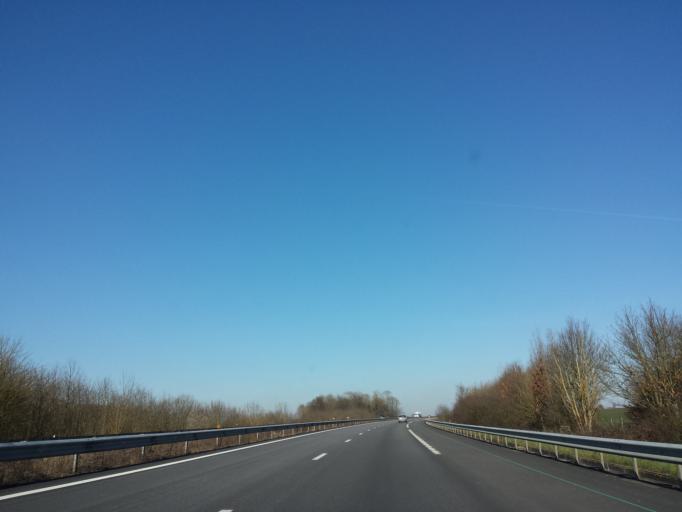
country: FR
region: Picardie
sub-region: Departement de l'Oise
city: Saint-Crepin-Ibouvillers
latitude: 49.2824
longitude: 2.0776
